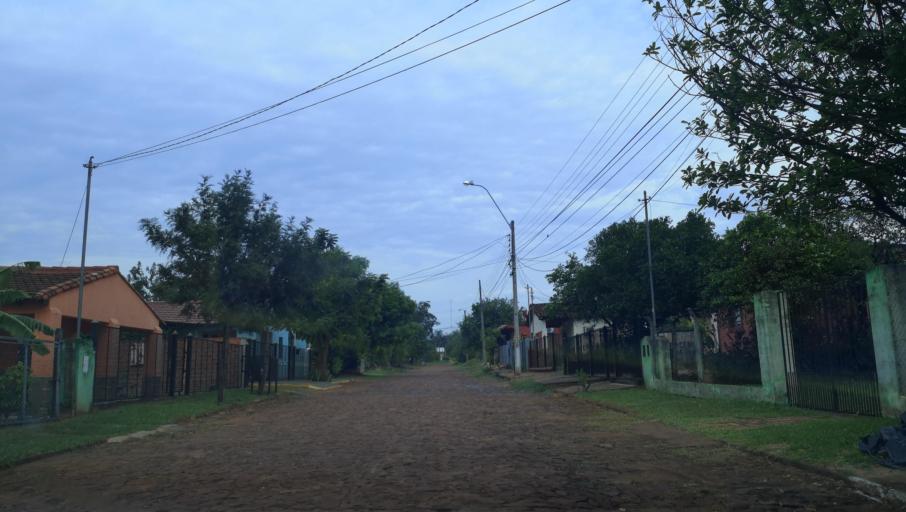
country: PY
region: Misiones
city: Santa Maria
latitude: -26.8806
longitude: -57.0251
